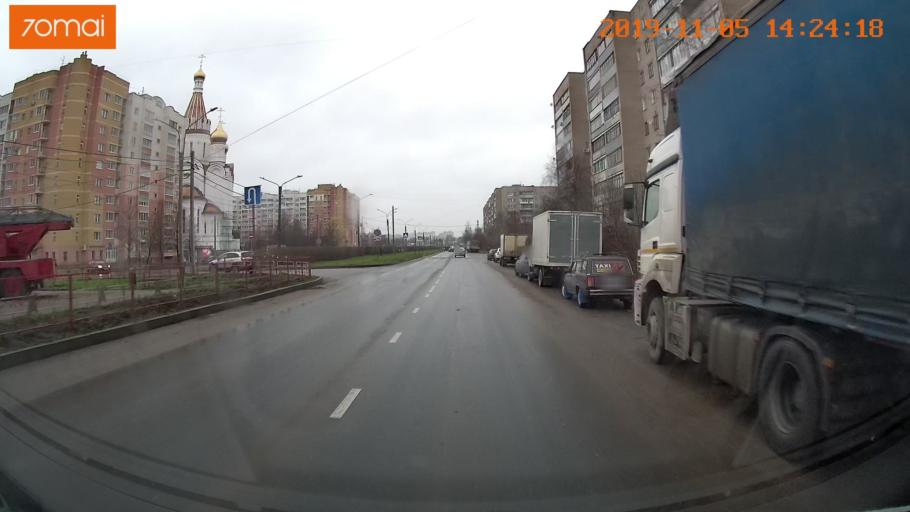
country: RU
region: Ivanovo
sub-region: Gorod Ivanovo
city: Ivanovo
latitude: 56.9680
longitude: 40.9981
